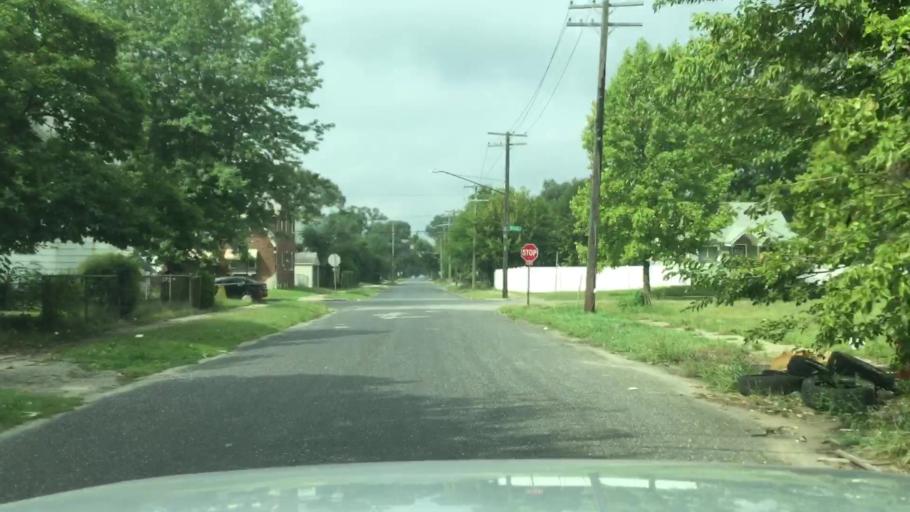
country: US
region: Michigan
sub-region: Oakland County
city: Oak Park
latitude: 42.4042
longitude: -83.1624
